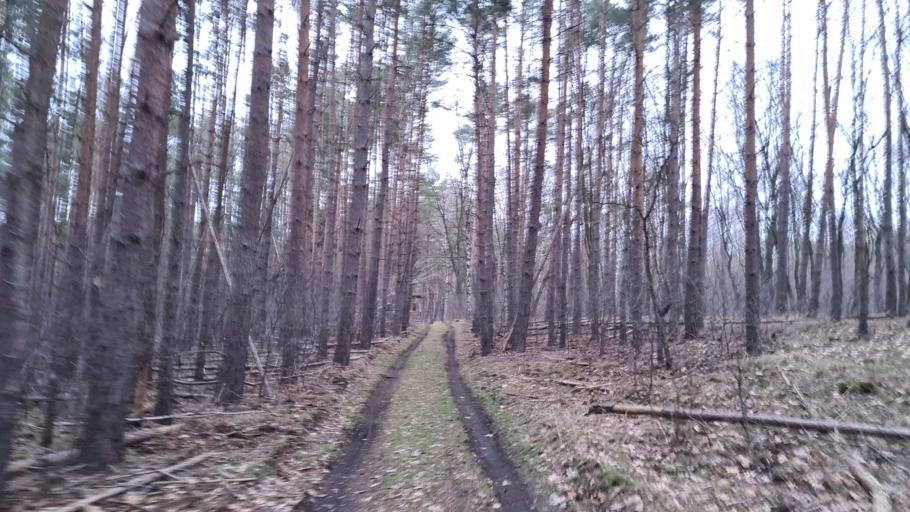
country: DE
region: Brandenburg
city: Trobitz
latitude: 51.5846
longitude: 13.4557
